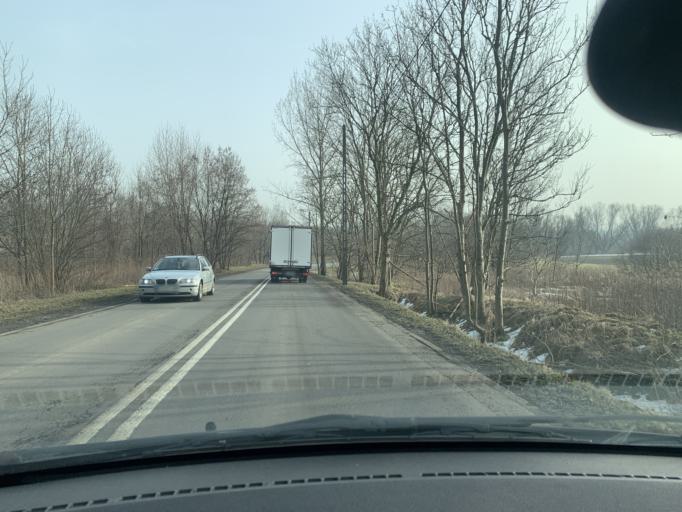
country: PL
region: Silesian Voivodeship
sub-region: Piekary Slaskie
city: Piekary Slaskie
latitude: 50.3679
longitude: 18.9145
